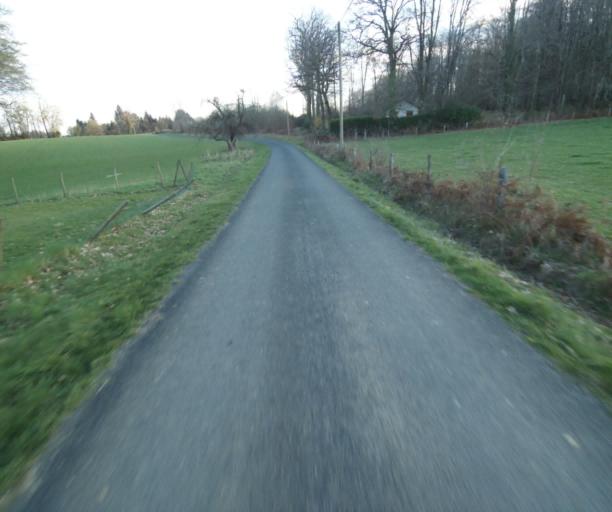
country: FR
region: Limousin
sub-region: Departement de la Correze
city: Uzerche
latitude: 45.3716
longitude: 1.5949
